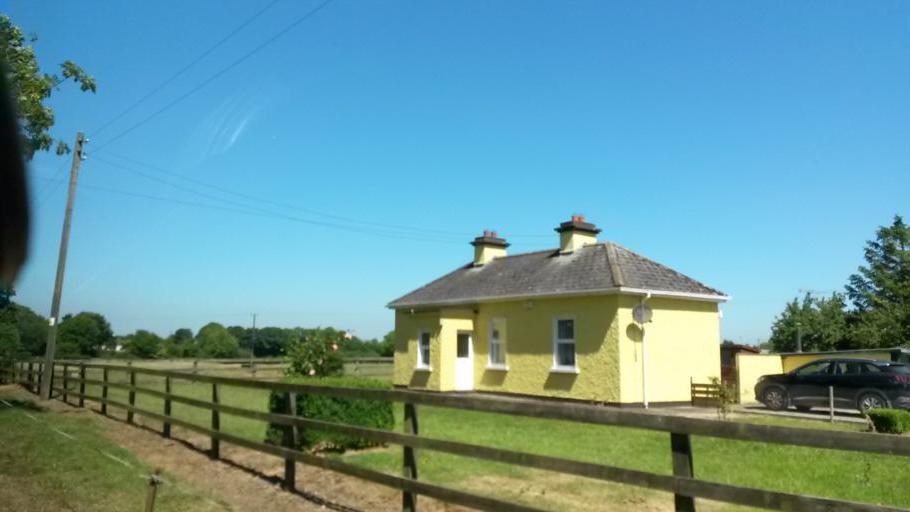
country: IE
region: Leinster
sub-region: Dublin City
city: Finglas
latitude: 53.4369
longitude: -6.3041
